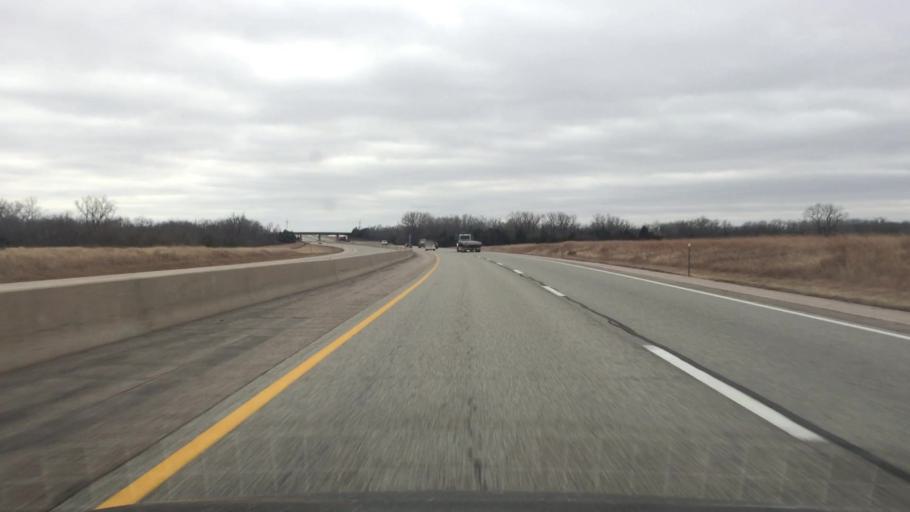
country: US
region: Kansas
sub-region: Butler County
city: El Dorado
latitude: 38.0473
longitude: -96.6398
